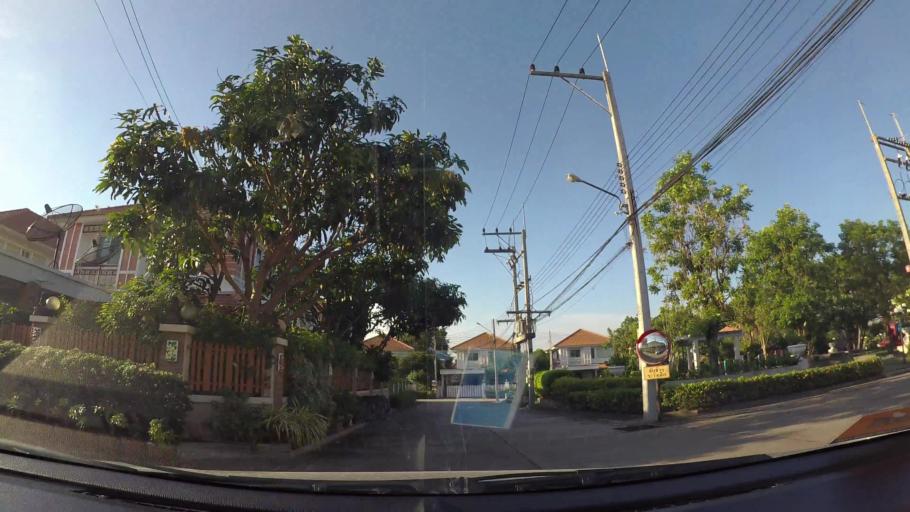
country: TH
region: Chon Buri
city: Si Racha
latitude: 13.1374
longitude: 100.9347
